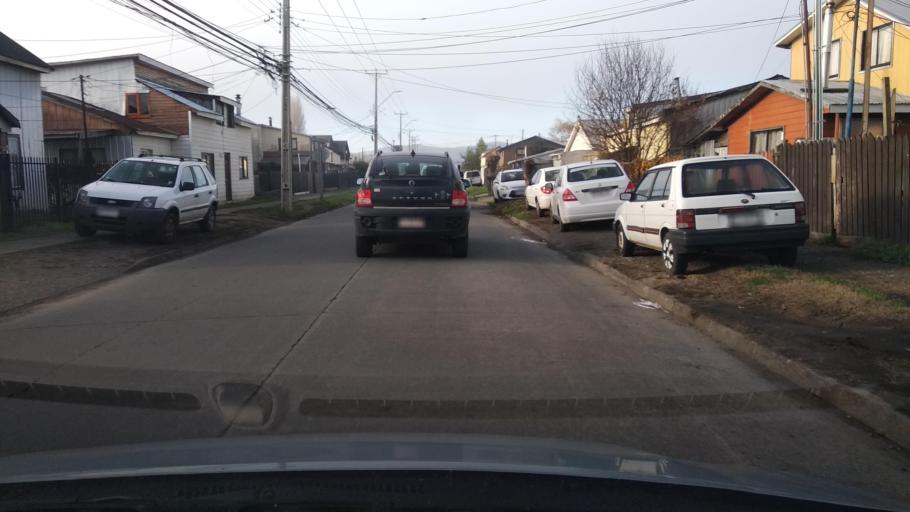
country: CL
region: Los Lagos
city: Las Animas
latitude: -39.8099
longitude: -73.2263
